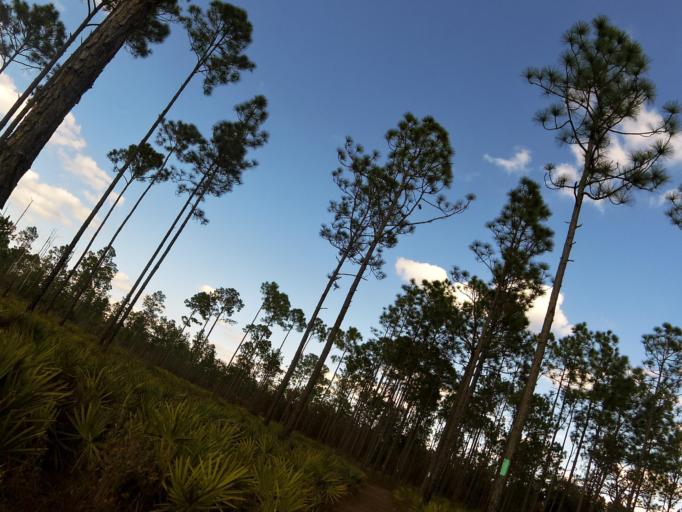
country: US
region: Florida
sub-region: Clay County
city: Middleburg
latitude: 30.1370
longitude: -81.9586
